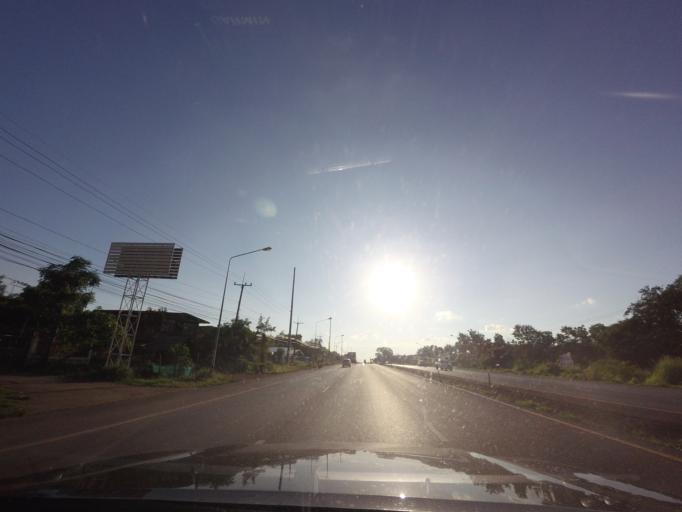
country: TH
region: Changwat Udon Thani
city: Ban Na Muang
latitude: 17.3526
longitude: 102.9280
